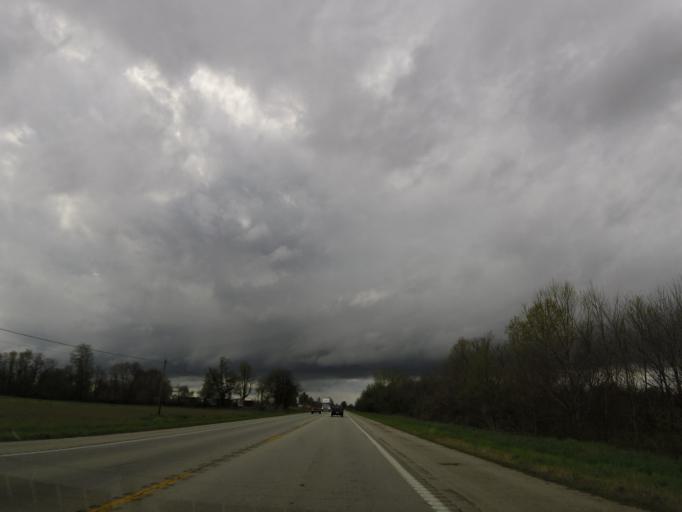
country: US
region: Arkansas
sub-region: Clay County
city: Corning
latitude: 36.5380
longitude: -90.5296
